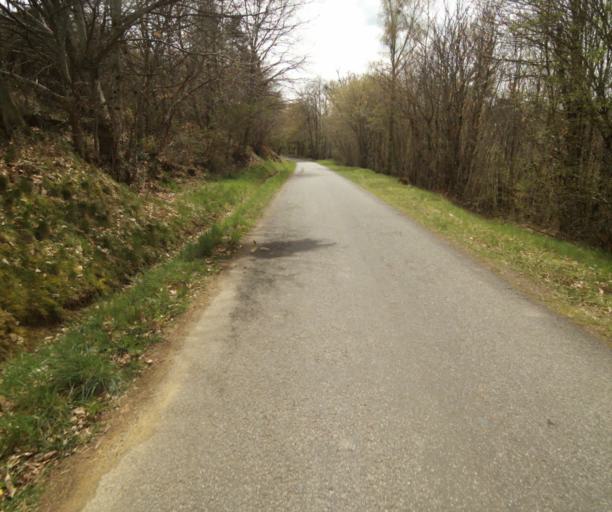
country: FR
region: Limousin
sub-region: Departement de la Correze
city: Laguenne
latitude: 45.2175
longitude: 1.8665
